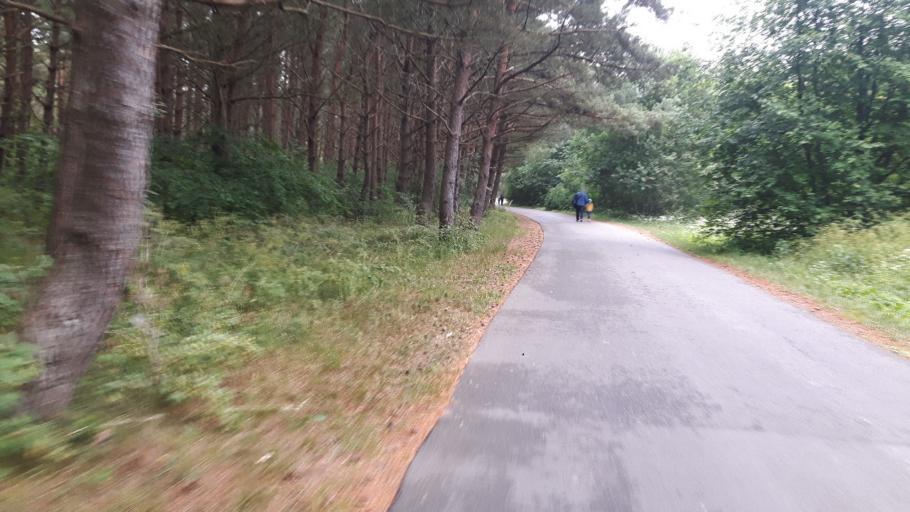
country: LT
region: Klaipedos apskritis
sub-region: Palanga
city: Sventoji
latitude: 56.0062
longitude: 21.0757
